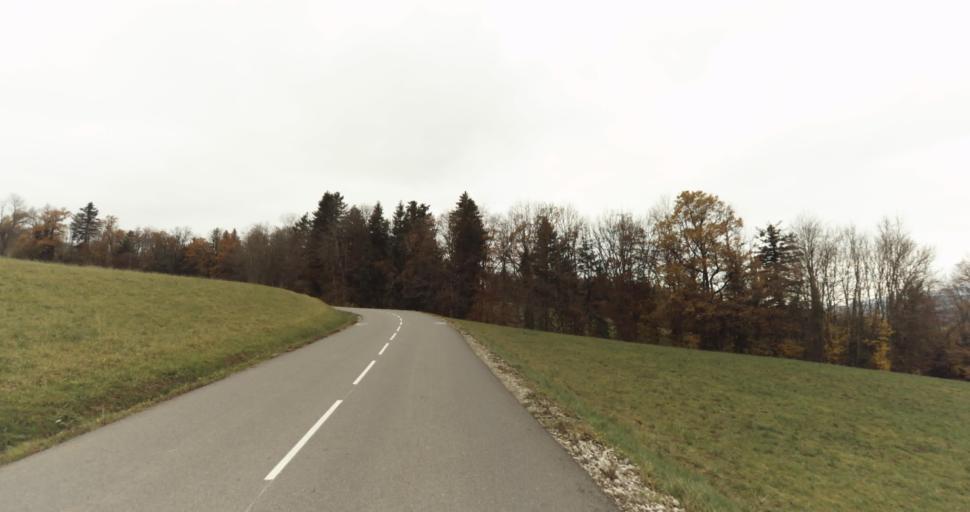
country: FR
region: Rhone-Alpes
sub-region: Departement de la Haute-Savoie
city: Thorens-Glieres
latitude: 45.9882
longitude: 6.2404
